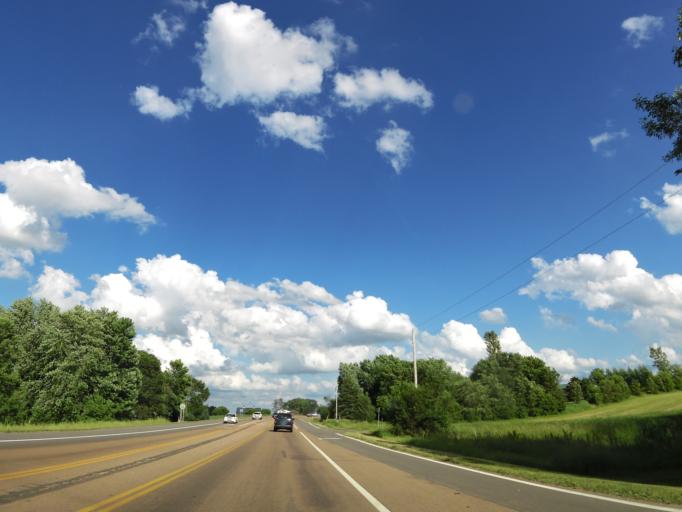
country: US
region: Minnesota
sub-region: Carver County
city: Victoria
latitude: 44.8105
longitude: -93.6645
